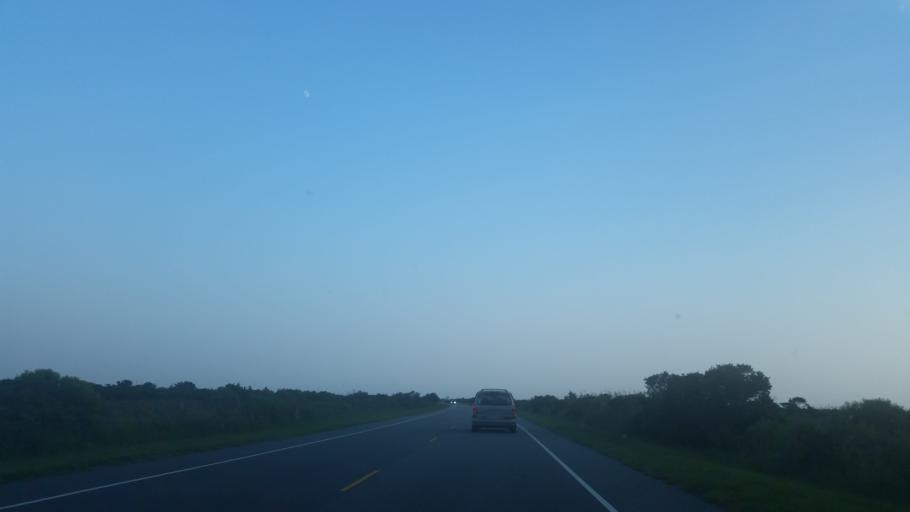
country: US
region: North Carolina
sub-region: Dare County
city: Wanchese
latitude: 35.8893
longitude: -75.5924
